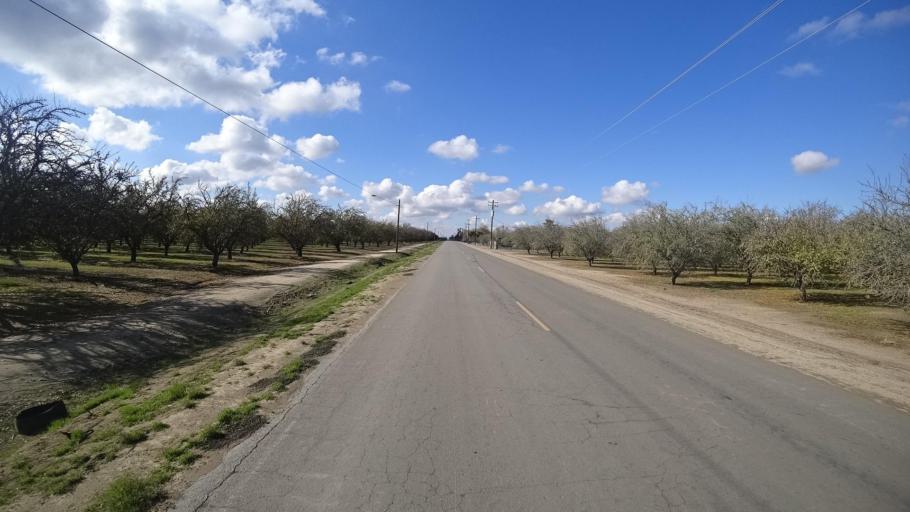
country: US
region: California
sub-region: Kern County
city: McFarland
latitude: 35.6887
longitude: -119.2614
